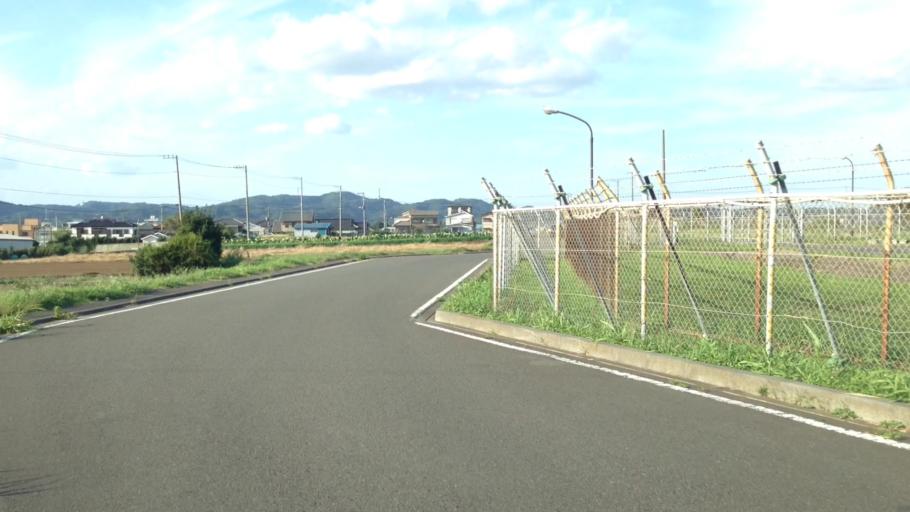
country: JP
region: Kanagawa
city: Miura
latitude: 35.2009
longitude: 139.6143
